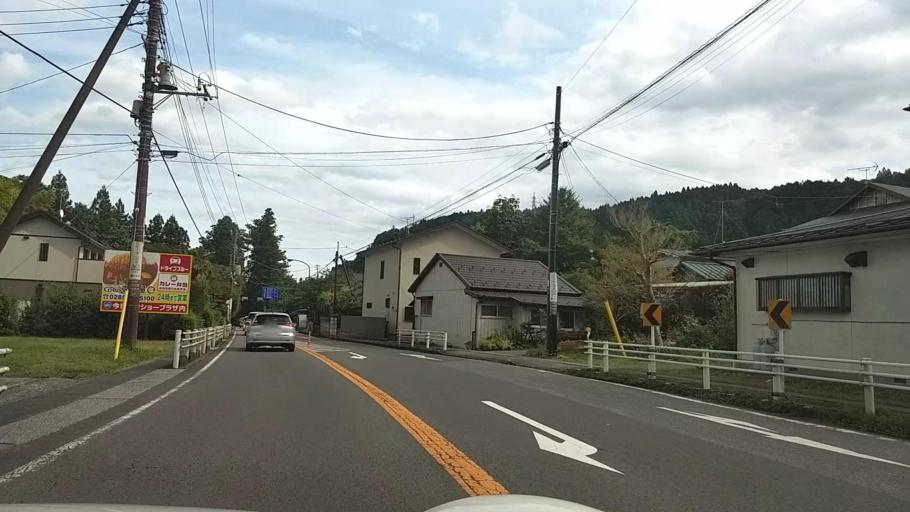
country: JP
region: Tochigi
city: Nikko
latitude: 36.7430
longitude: 139.6288
